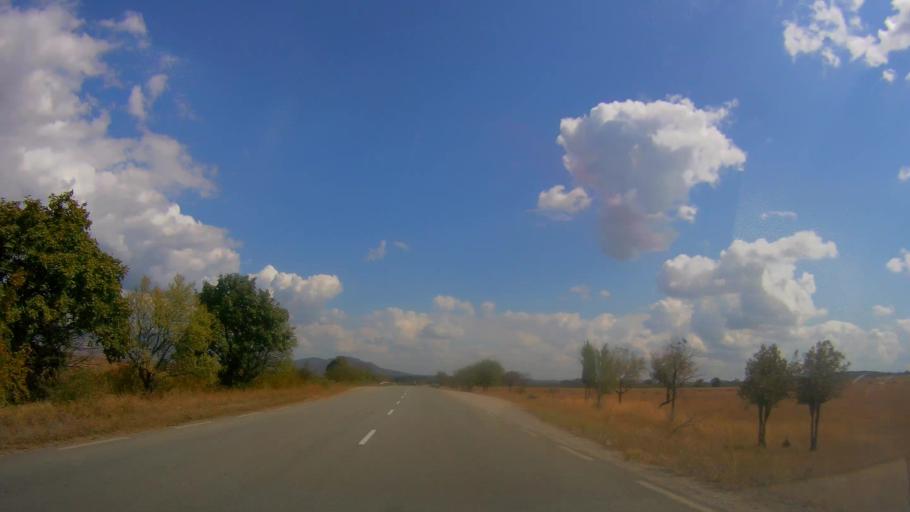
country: BG
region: Sliven
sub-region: Obshtina Tvurditsa
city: Tvurditsa
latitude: 42.6546
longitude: 25.9423
